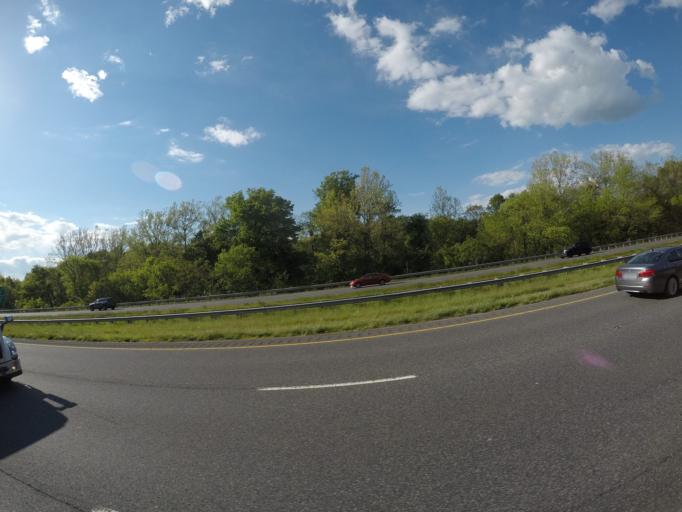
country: US
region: Maryland
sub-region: Carroll County
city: Mount Airy
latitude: 39.3596
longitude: -77.1539
